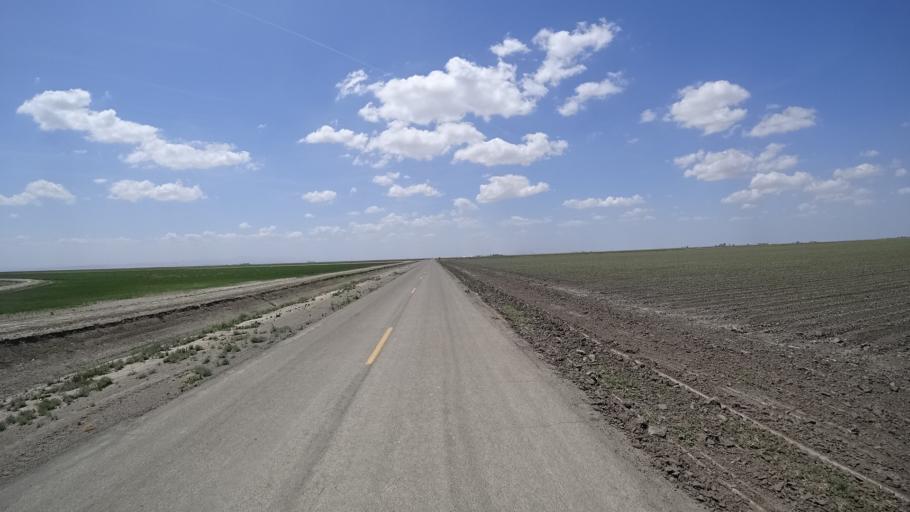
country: US
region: California
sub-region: Kings County
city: Stratford
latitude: 36.1526
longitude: -119.8210
